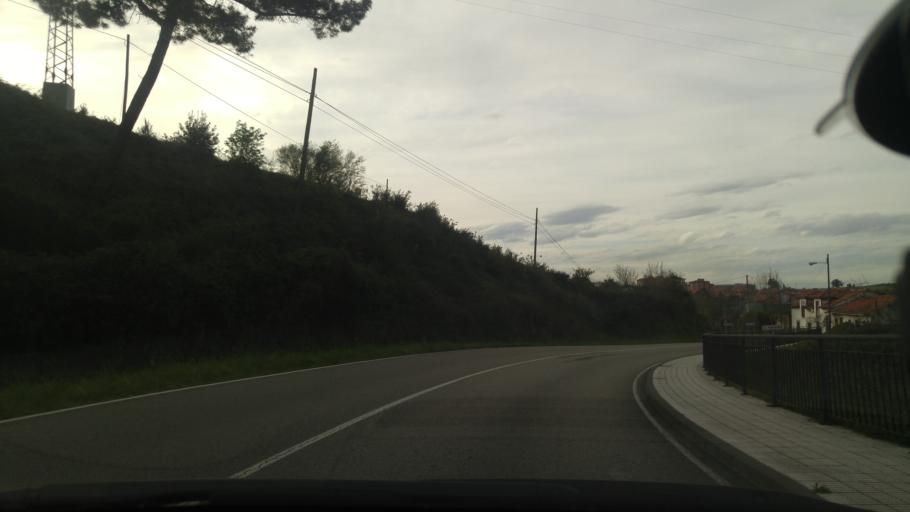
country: ES
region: Asturias
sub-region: Province of Asturias
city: Corvera de Asturias
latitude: 43.5302
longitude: -5.8811
